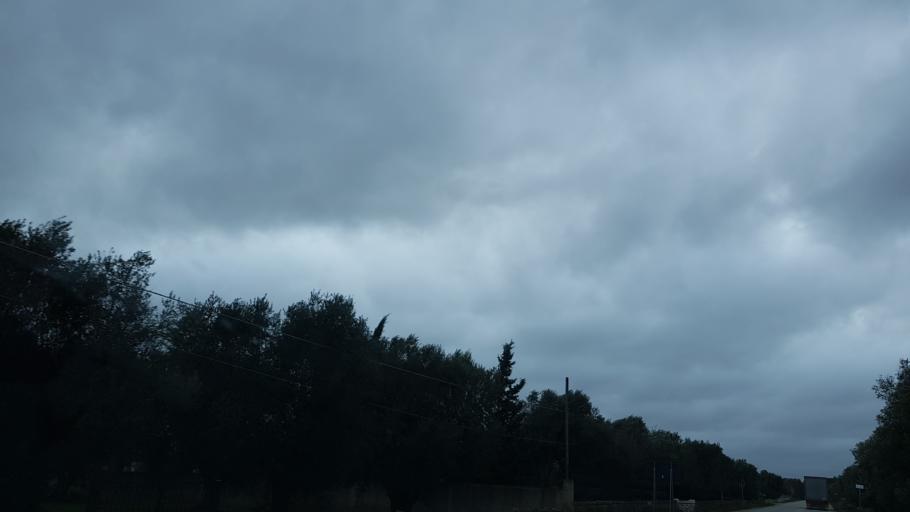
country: IT
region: Apulia
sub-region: Provincia di Brindisi
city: San Vito dei Normanni
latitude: 40.6540
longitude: 17.7757
